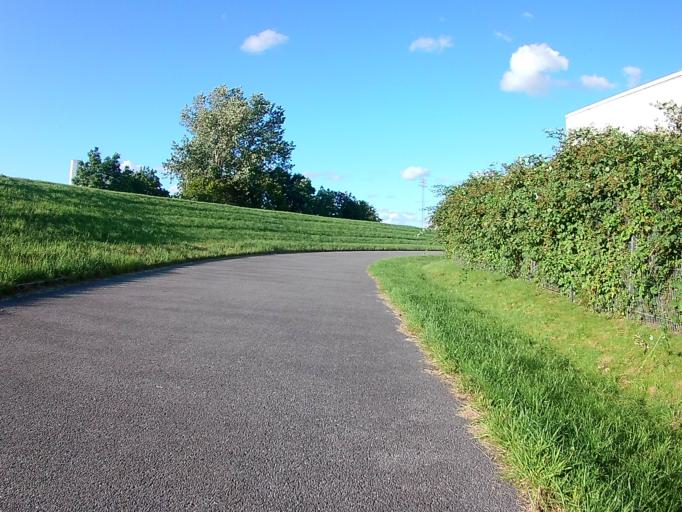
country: DE
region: Hamburg
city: Harburg
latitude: 53.4702
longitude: 9.9761
